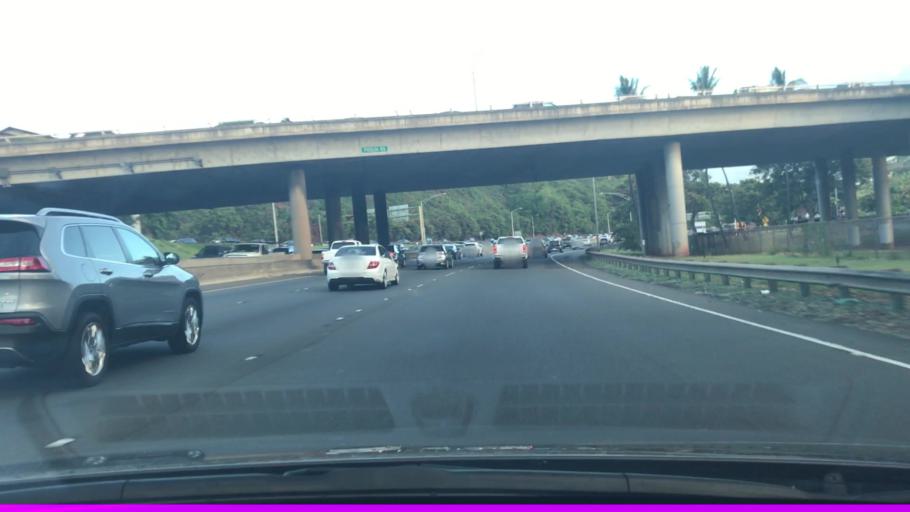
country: US
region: Hawaii
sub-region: Honolulu County
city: Halawa Heights
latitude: 21.3486
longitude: -157.8956
